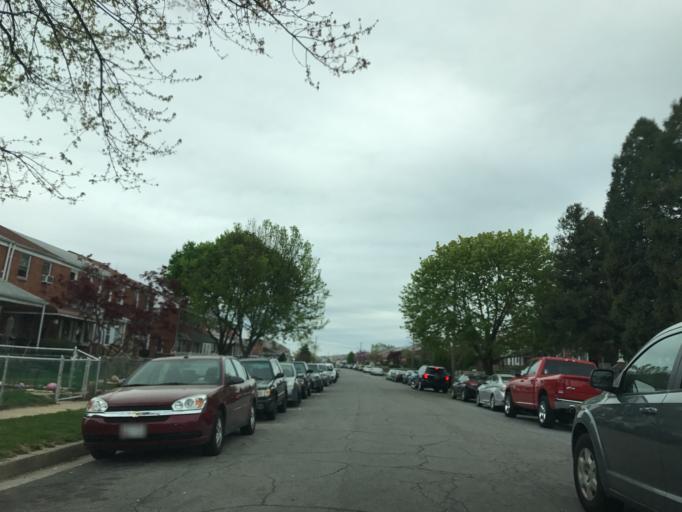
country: US
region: Maryland
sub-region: Baltimore County
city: Middle River
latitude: 39.3268
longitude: -76.4597
